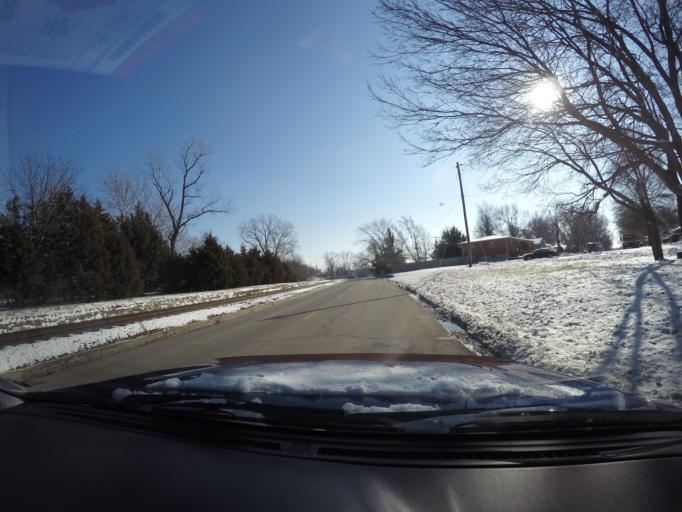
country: US
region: Kansas
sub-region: Johnson County
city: Olathe
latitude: 38.8719
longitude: -94.8171
